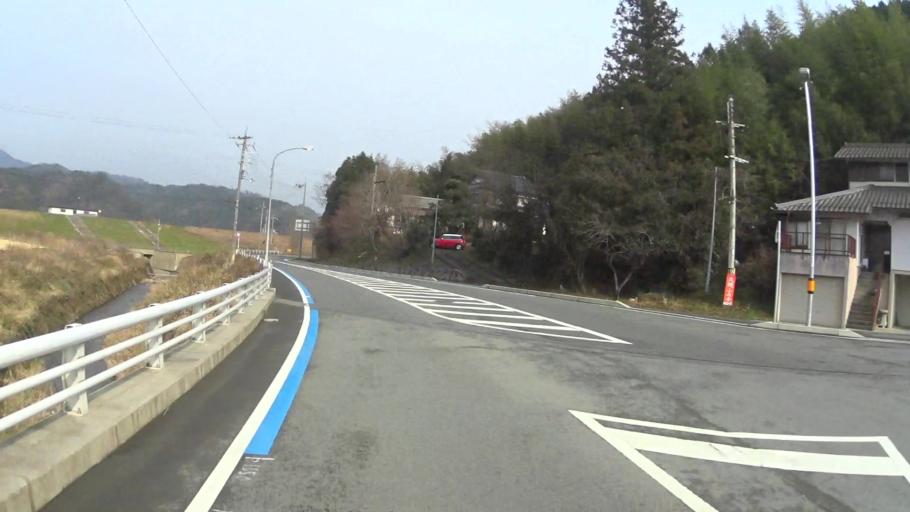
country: JP
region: Kyoto
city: Fukuchiyama
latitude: 35.3770
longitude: 135.1422
